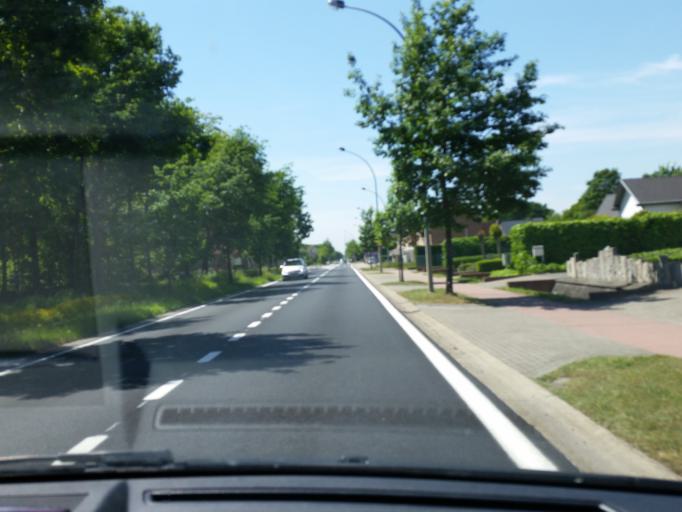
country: BE
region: Flanders
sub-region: Provincie Antwerpen
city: Bonheiden
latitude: 51.0360
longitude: 4.5377
